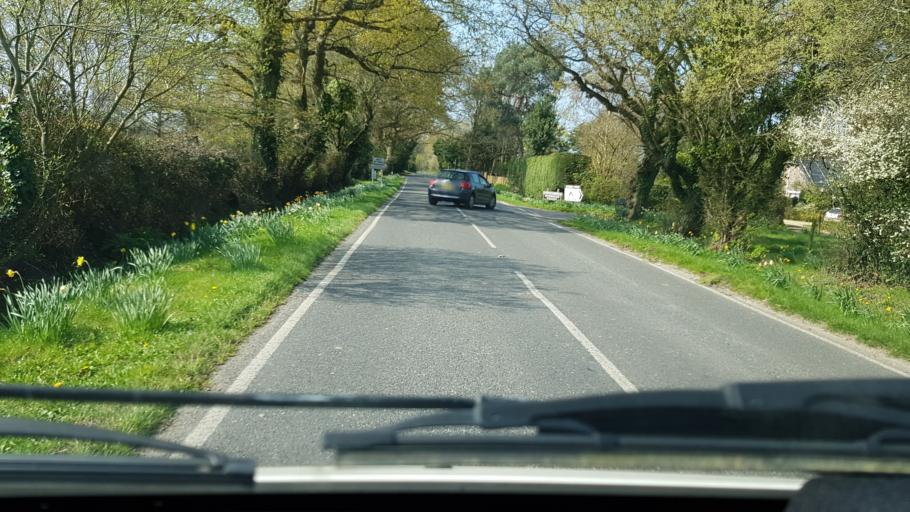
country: GB
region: England
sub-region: West Sussex
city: East Wittering
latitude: 50.7873
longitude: -0.8694
